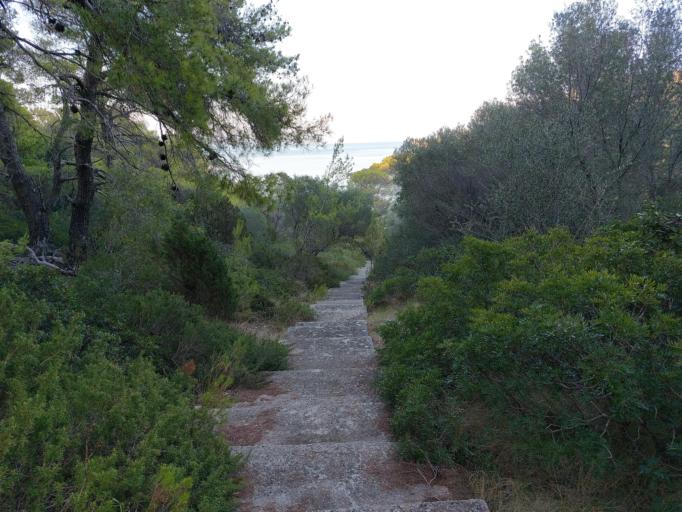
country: HR
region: Dubrovacko-Neretvanska
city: Smokvica
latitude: 42.7708
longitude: 16.7916
